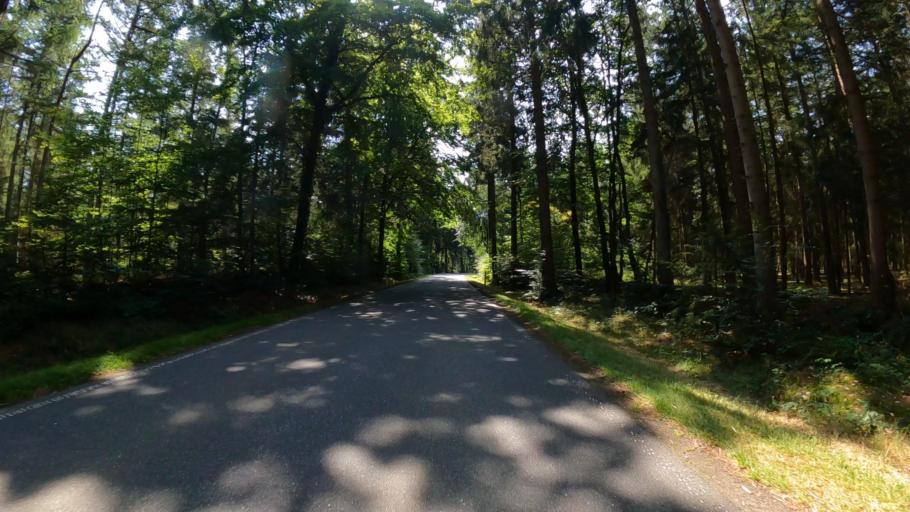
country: DE
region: Schleswig-Holstein
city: Heidmuhlen
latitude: 53.9544
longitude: 10.1378
